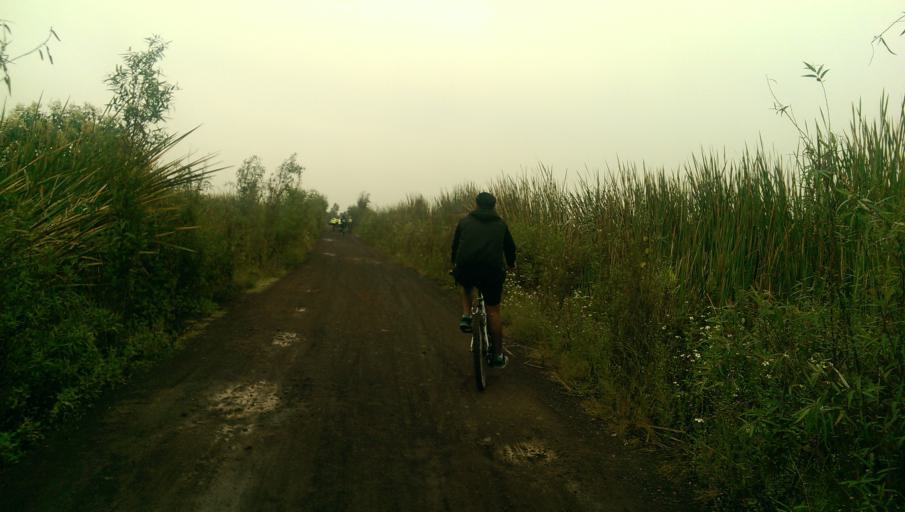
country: MX
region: Mexico City
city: Xochimilco
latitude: 19.2689
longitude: -99.0608
